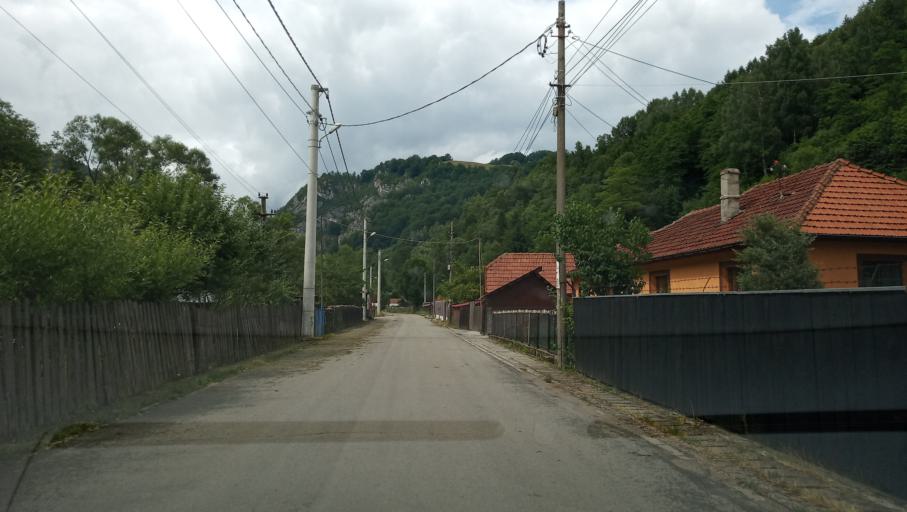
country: RO
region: Hunedoara
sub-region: Oras Petrila
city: Petrila
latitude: 45.4622
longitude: 23.4201
